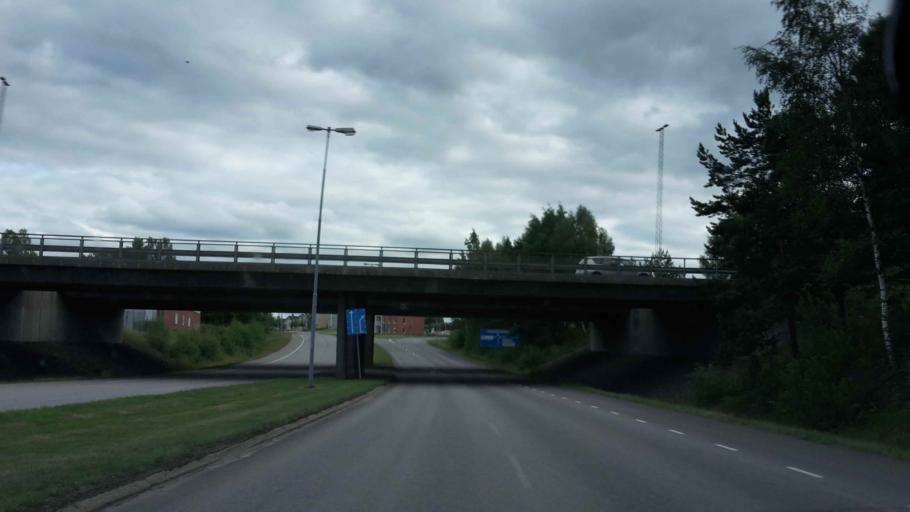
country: SE
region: OEstergoetland
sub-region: Norrkopings Kommun
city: Norrkoping
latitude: 58.5833
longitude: 16.1399
